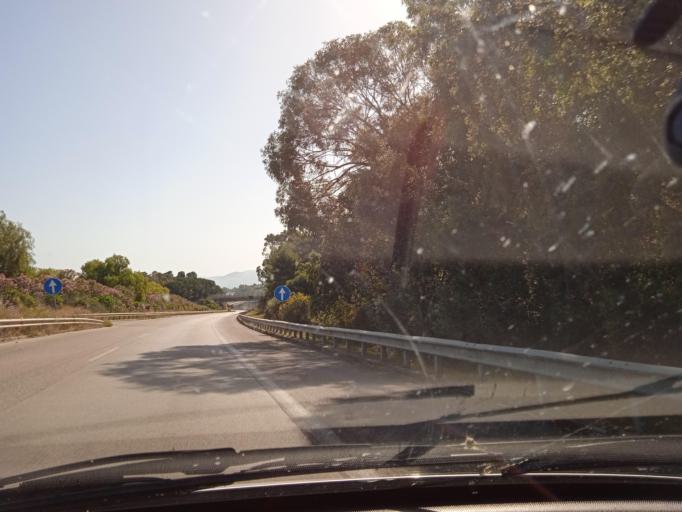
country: IT
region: Sicily
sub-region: Messina
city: Acquedolci
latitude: 38.0445
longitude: 14.5503
